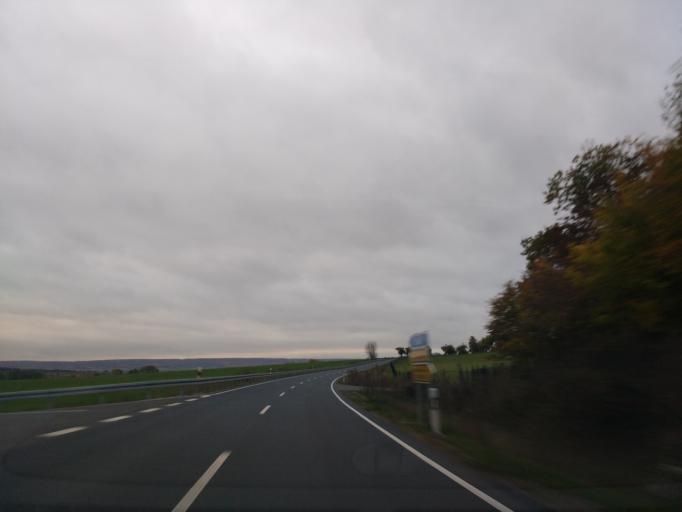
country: DE
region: Thuringia
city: Buhla
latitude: 51.4325
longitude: 10.4435
